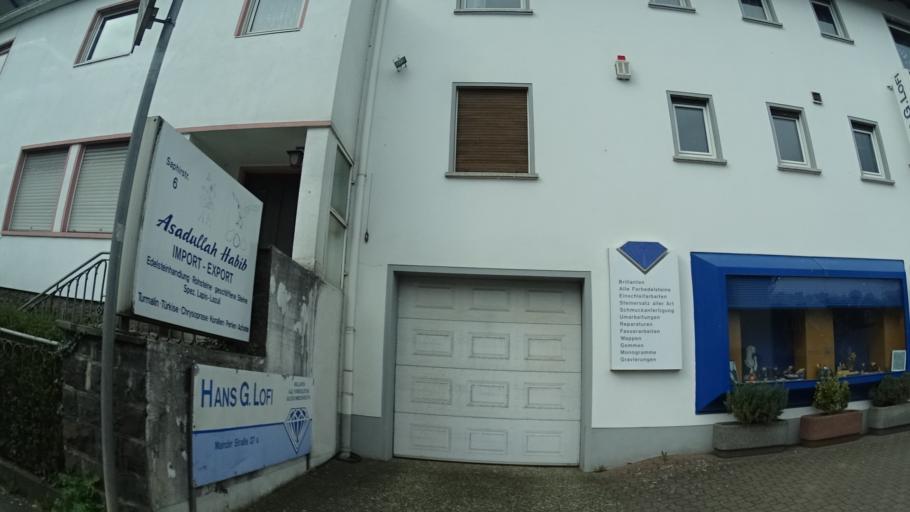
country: DE
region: Rheinland-Pfalz
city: Idar-Oberstein
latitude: 49.7204
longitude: 7.2992
